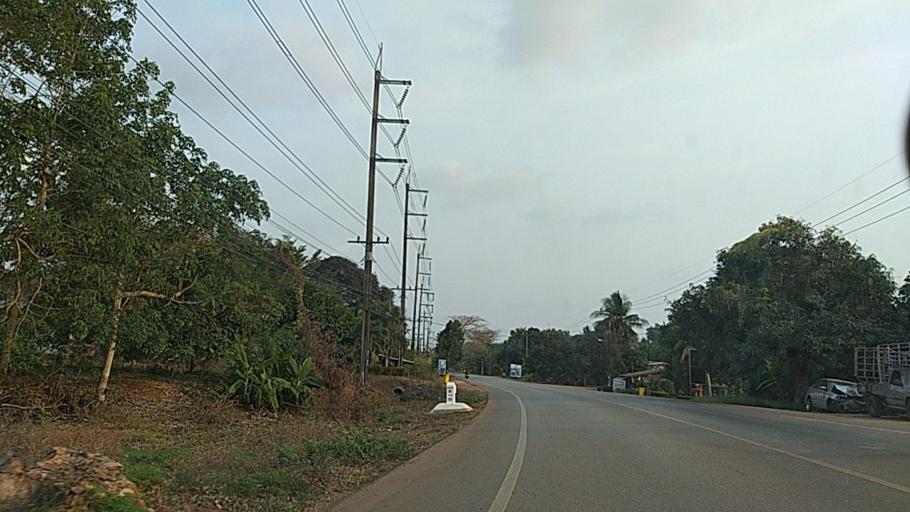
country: TH
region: Trat
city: Laem Ngop
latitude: 12.2421
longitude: 102.2945
